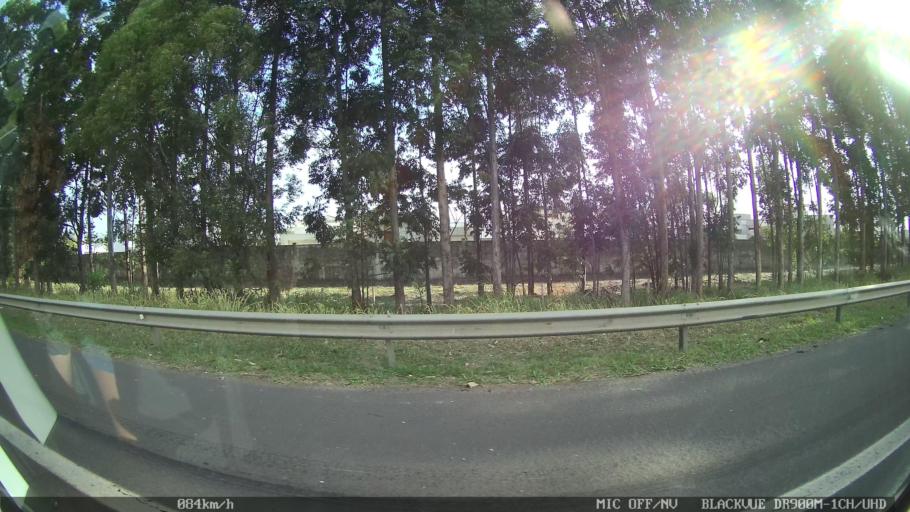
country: BR
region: Sao Paulo
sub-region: Paulinia
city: Paulinia
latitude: -22.7708
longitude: -47.1370
